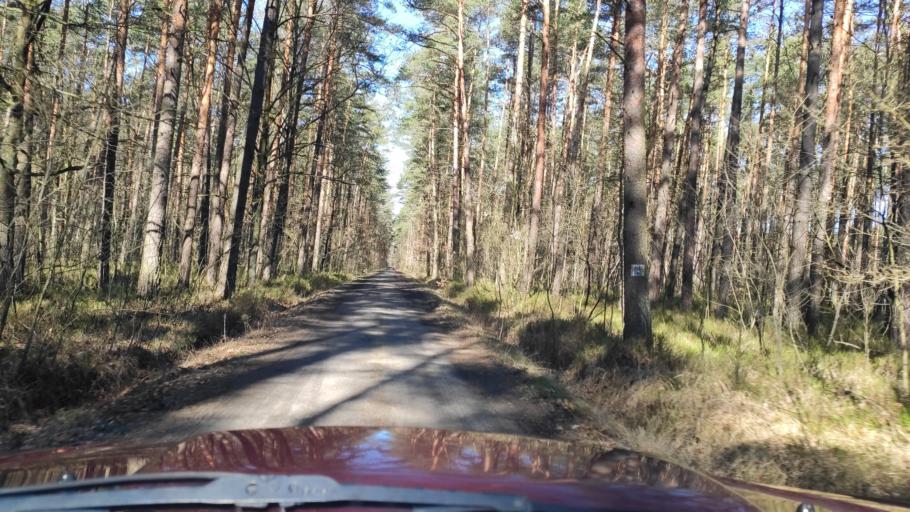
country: PL
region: Masovian Voivodeship
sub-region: Powiat kozienicki
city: Garbatka-Letnisko
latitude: 51.4360
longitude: 21.5456
